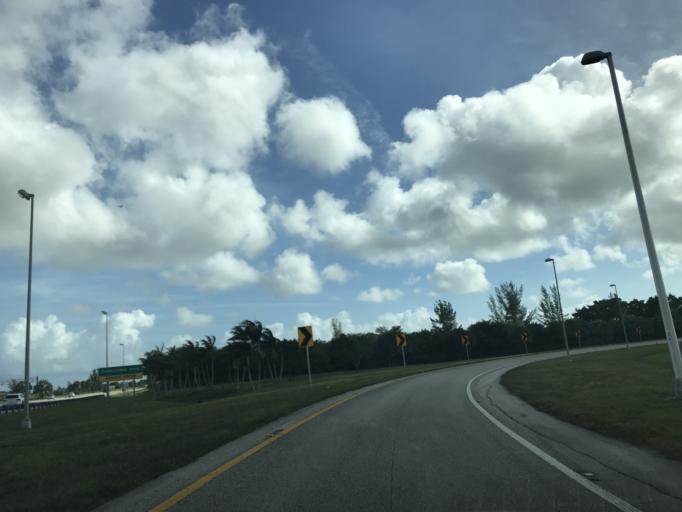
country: US
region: Florida
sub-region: Palm Beach County
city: Boca Pointe
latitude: 26.3052
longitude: -80.1672
